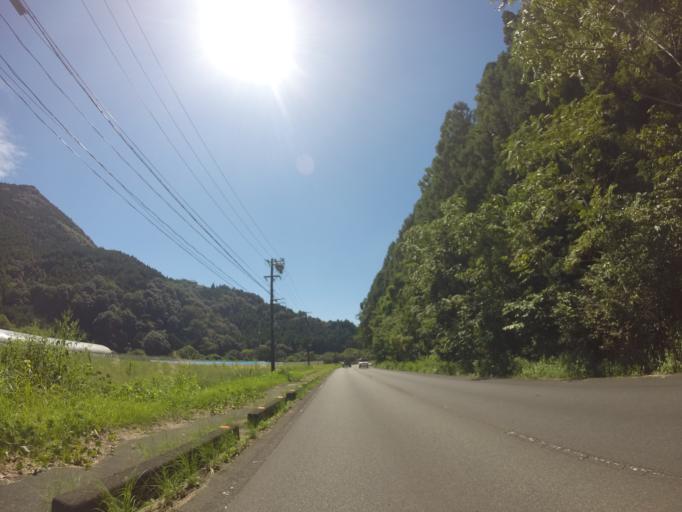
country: JP
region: Shizuoka
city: Fujieda
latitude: 34.9517
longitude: 138.2119
